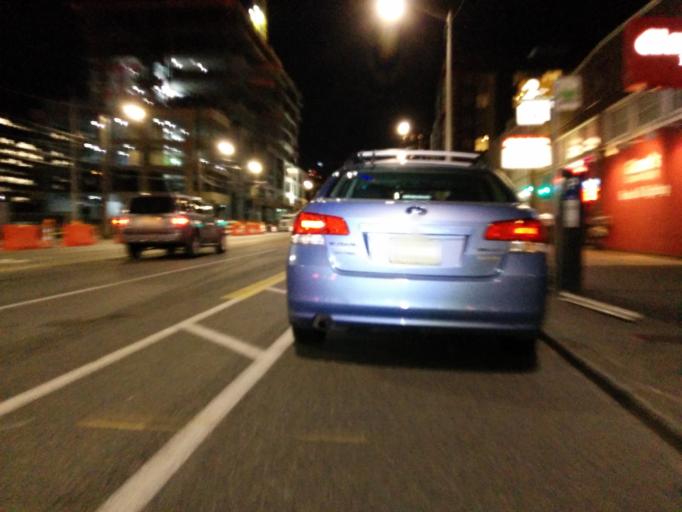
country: US
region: Washington
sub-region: King County
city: Seattle
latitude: 47.6239
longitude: -122.3425
